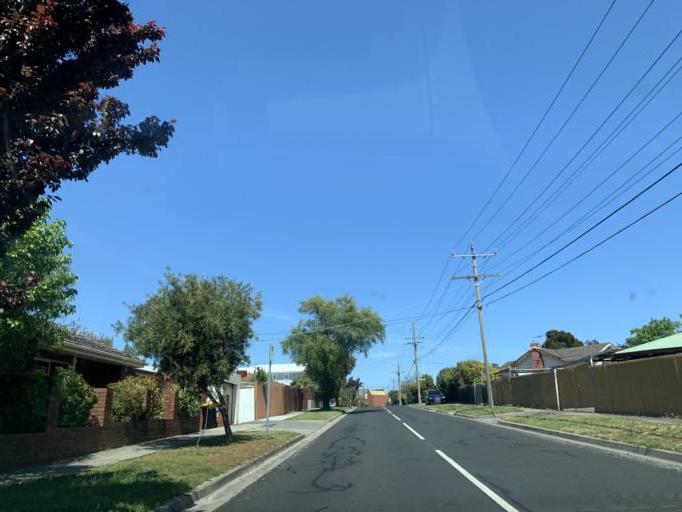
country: AU
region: Victoria
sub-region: Bayside
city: Moorabbin
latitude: -37.9395
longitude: 145.0420
